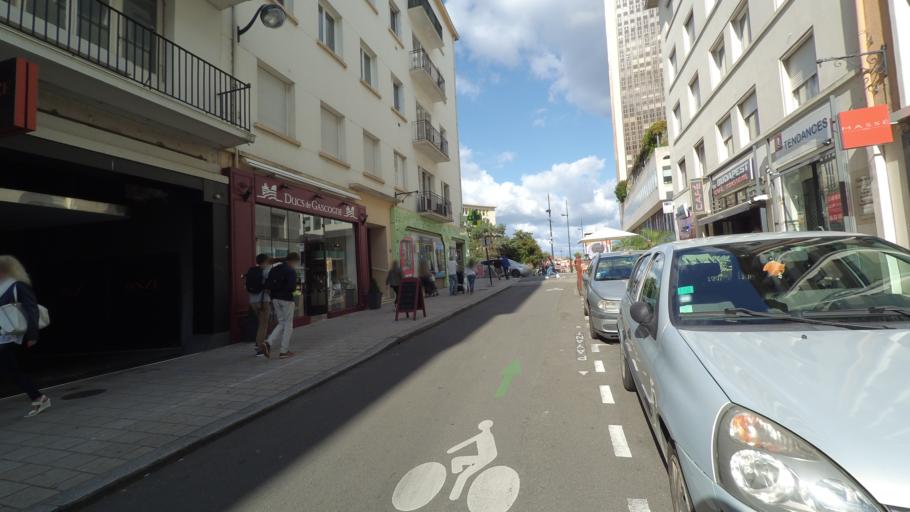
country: FR
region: Pays de la Loire
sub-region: Departement de la Loire-Atlantique
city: Nantes
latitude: 47.2168
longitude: -1.5598
